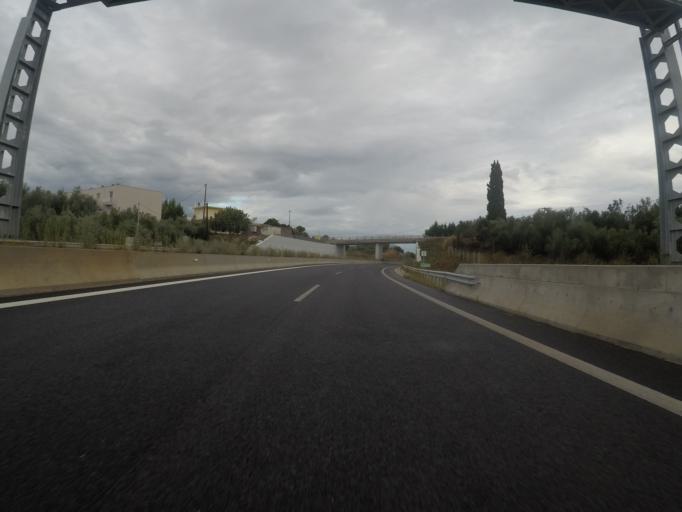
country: GR
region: Peloponnese
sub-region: Nomos Messinias
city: Sperkhoyia
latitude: 37.0596
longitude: 22.0687
